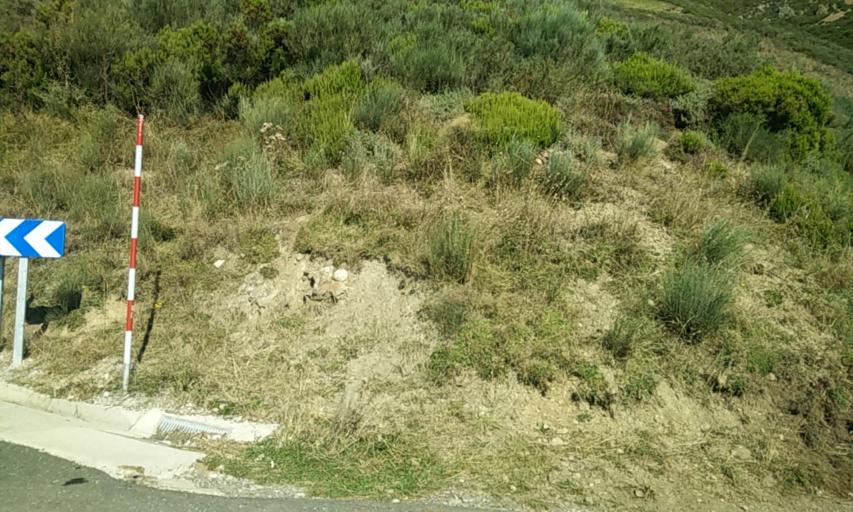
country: ES
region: Cantabria
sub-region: Provincia de Cantabria
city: Camaleno
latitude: 43.0768
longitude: -4.7331
